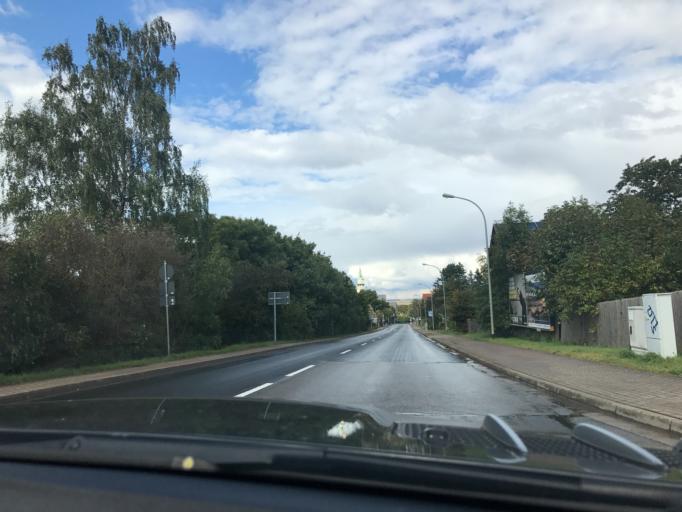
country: DE
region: Thuringia
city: Bad Langensalza
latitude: 51.1017
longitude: 10.6462
